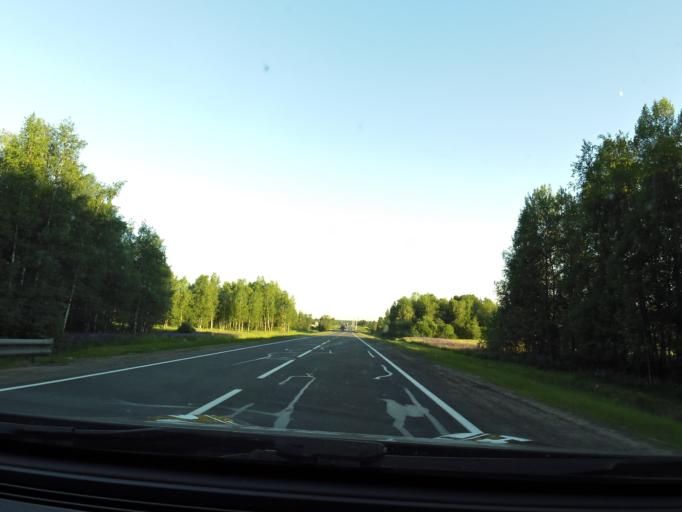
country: RU
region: Vologda
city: Gryazovets
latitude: 58.7137
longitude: 40.2968
